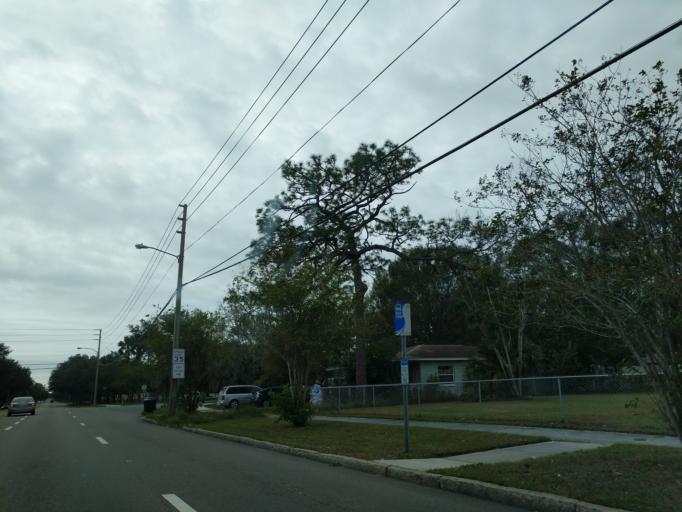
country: US
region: Florida
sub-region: Pinellas County
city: Lealman
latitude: 27.8209
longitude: -82.6469
